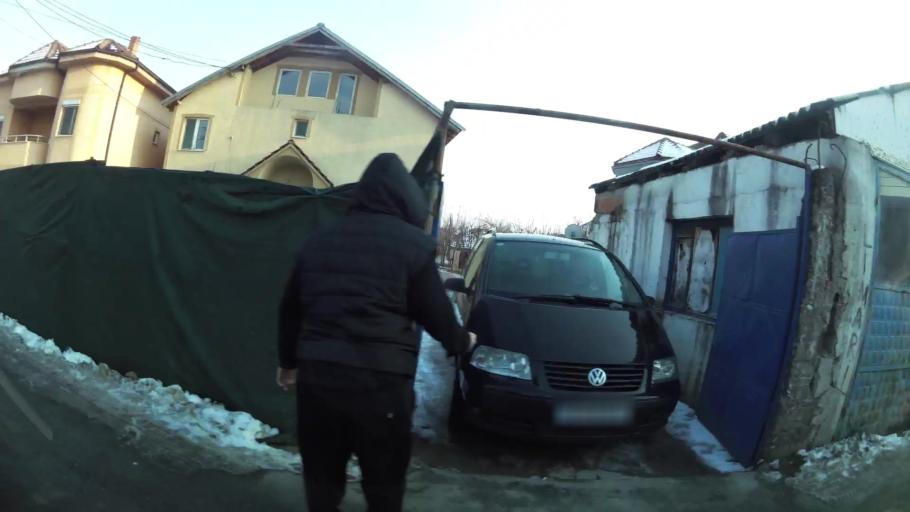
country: MK
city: Creshevo
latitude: 42.0206
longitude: 21.5150
